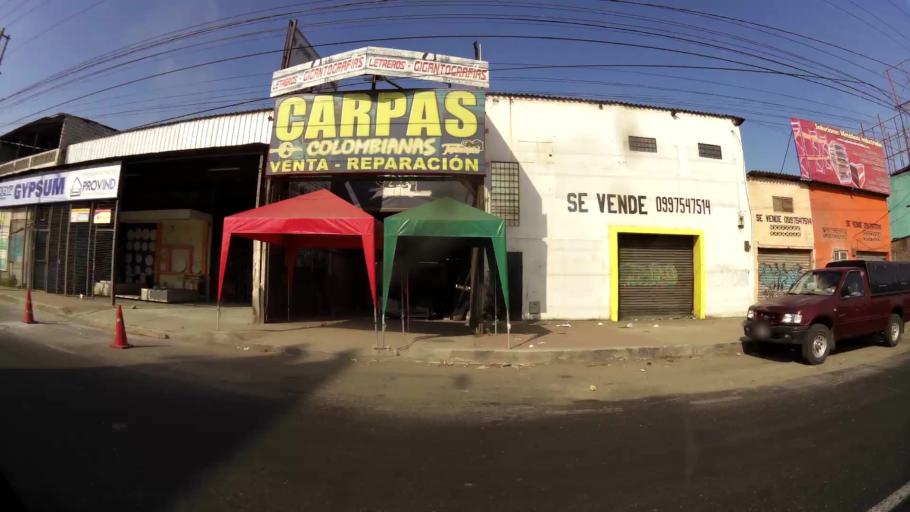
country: EC
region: Guayas
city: Eloy Alfaro
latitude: -2.1719
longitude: -79.8356
